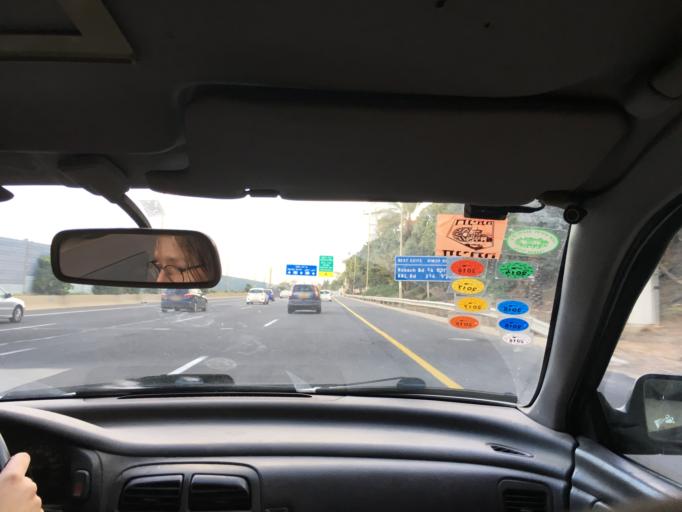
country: IL
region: Tel Aviv
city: Ramat Gan
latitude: 32.0896
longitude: 34.8008
